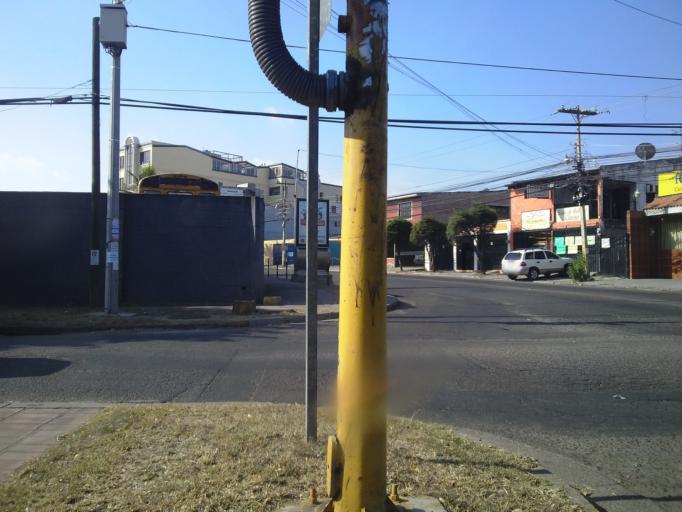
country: HN
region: Francisco Morazan
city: Tegucigalpa
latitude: 14.0781
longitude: -87.1913
